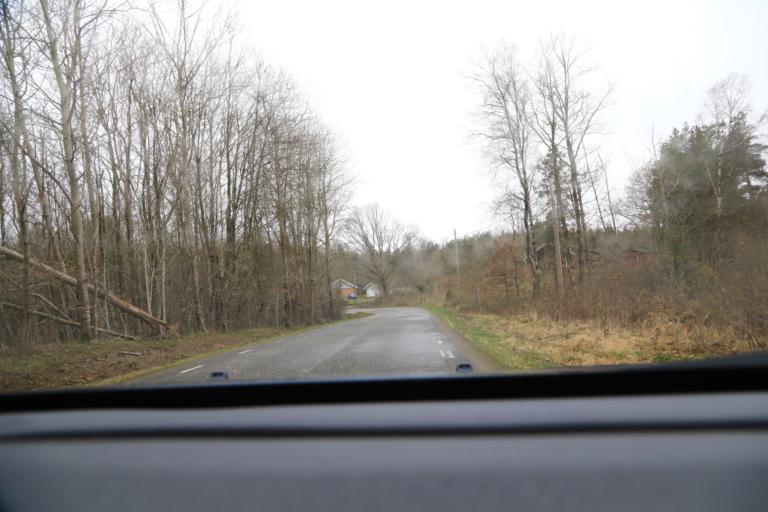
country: SE
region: Halland
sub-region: Kungsbacka Kommun
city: Frillesas
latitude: 57.2824
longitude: 12.2052
